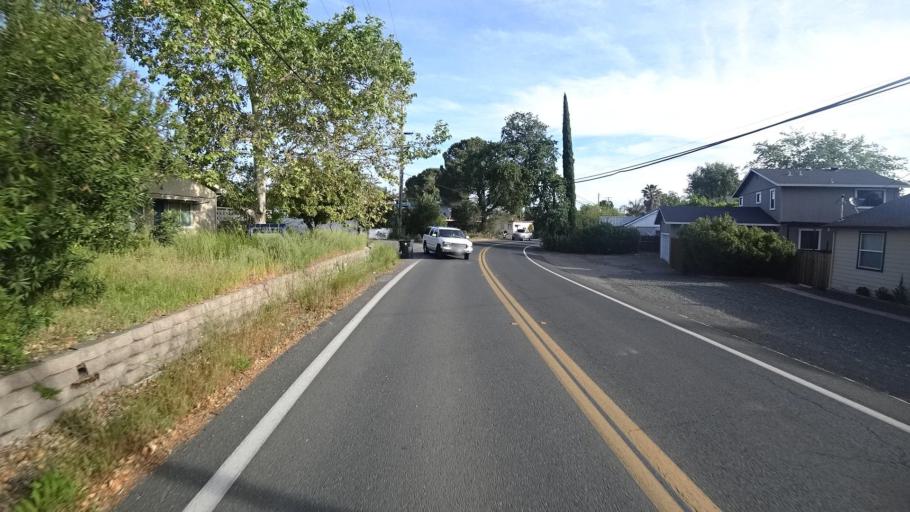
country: US
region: California
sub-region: Lake County
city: North Lakeport
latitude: 39.0891
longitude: -122.9034
